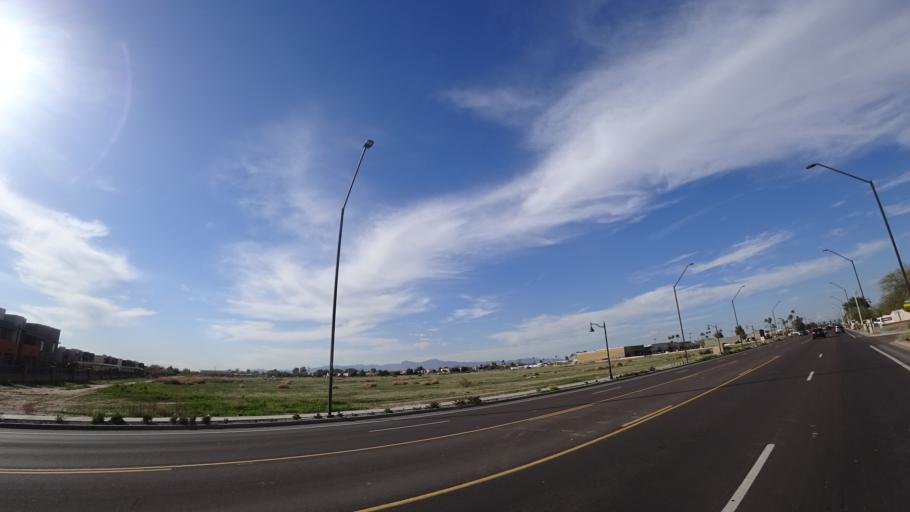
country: US
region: Arizona
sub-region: Maricopa County
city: Avondale
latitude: 33.4454
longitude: -112.3411
